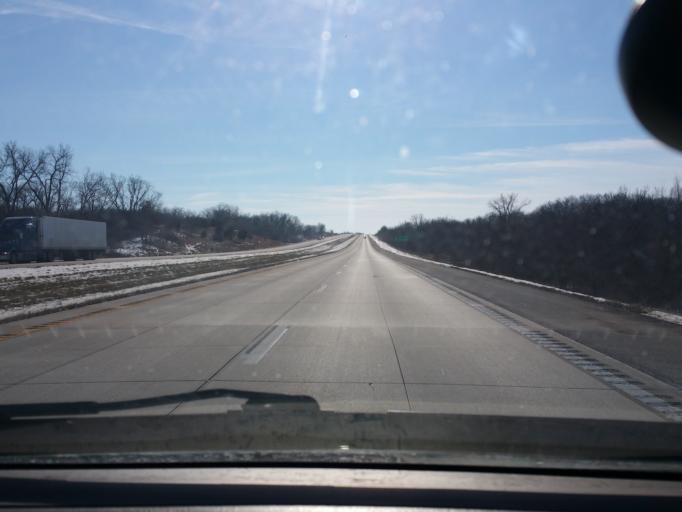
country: US
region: Missouri
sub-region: Daviess County
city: Gallatin
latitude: 39.9863
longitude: -94.0951
